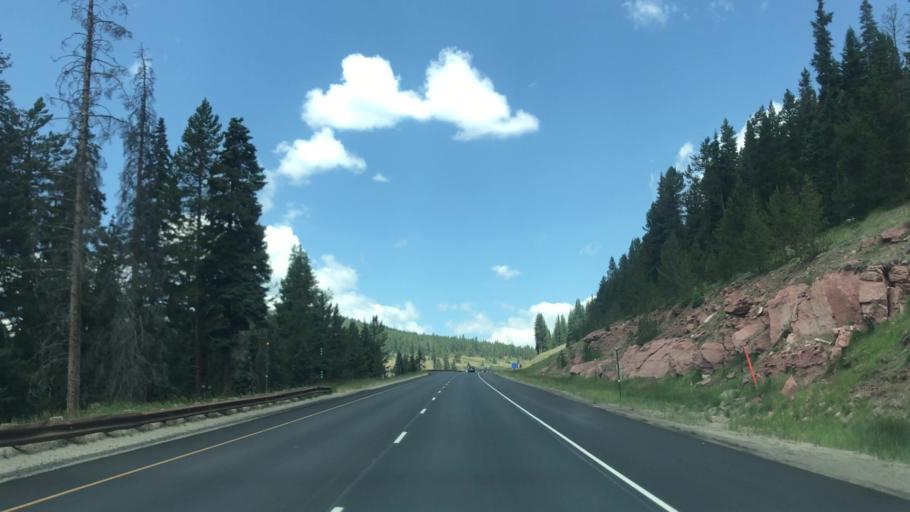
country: US
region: Colorado
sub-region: Summit County
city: Frisco
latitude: 39.5218
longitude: -106.2131
